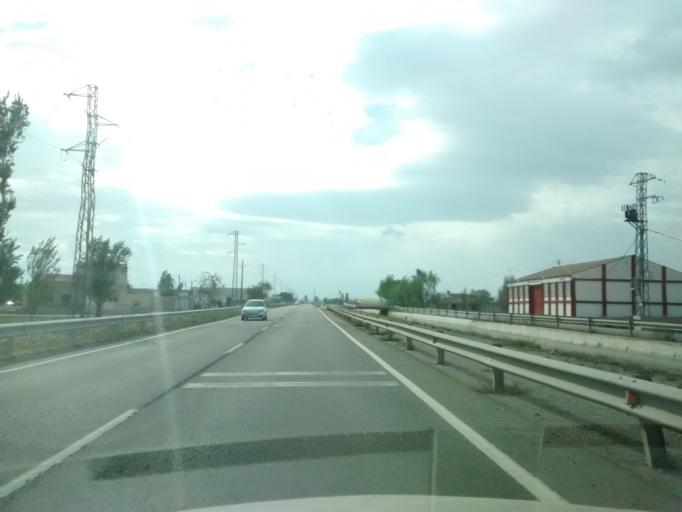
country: ES
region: Catalonia
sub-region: Provincia de Tarragona
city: Deltebre
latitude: 40.7261
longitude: 0.7116
